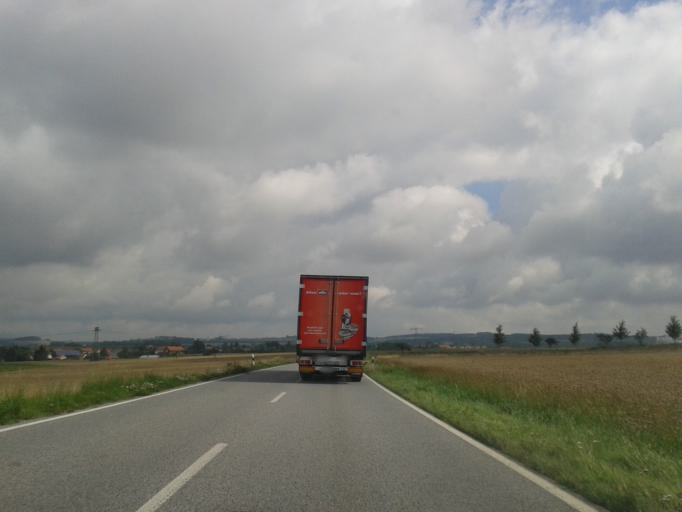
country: DE
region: Saxony
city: Lichtenberg
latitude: 51.1407
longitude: 13.9527
